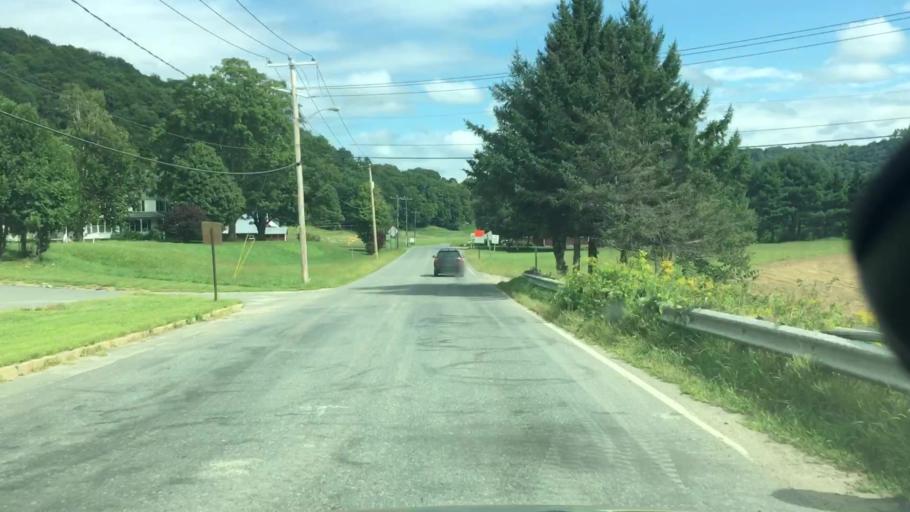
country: US
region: Massachusetts
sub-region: Franklin County
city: Colrain
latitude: 42.6757
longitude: -72.6960
